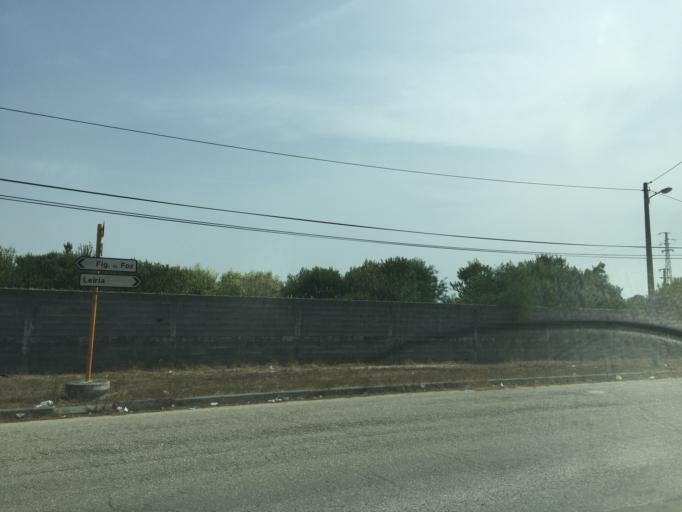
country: PT
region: Coimbra
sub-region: Figueira da Foz
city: Figueira da Foz
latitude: 40.1235
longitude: -8.8575
